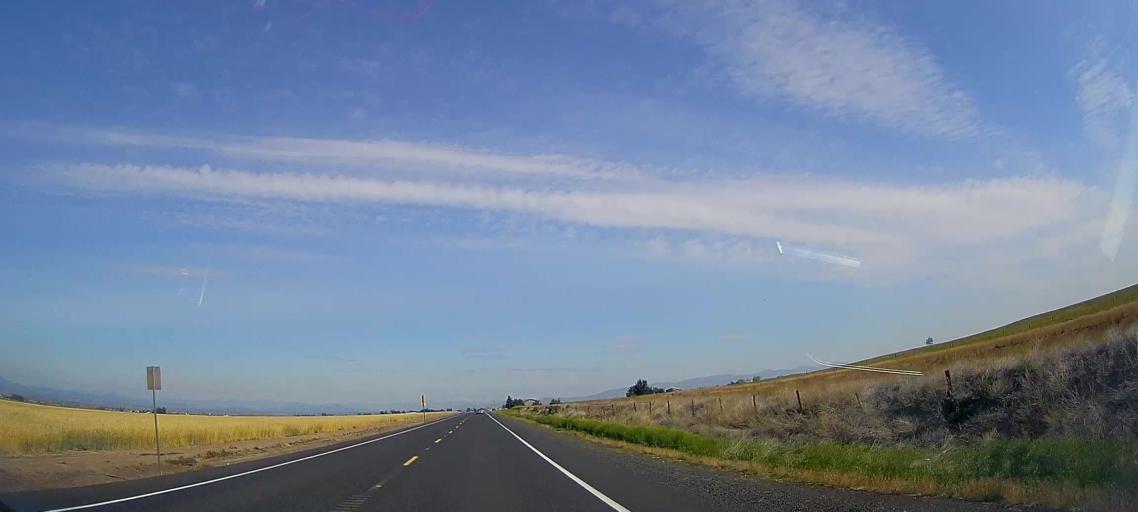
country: US
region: Oregon
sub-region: Jefferson County
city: Madras
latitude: 44.6708
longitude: -121.1403
